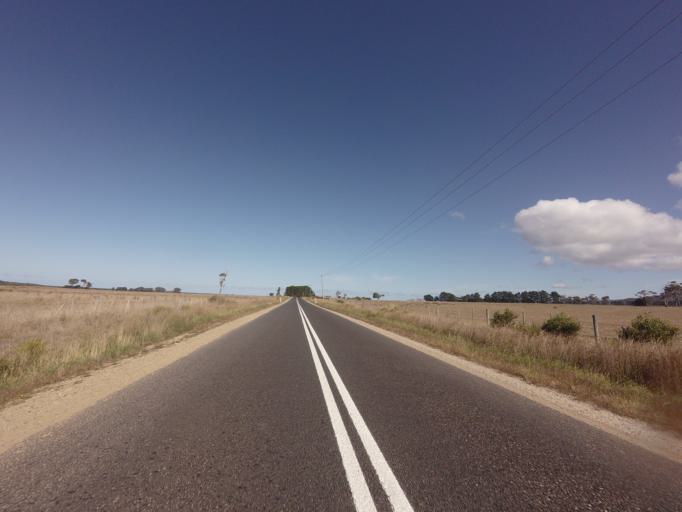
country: AU
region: Tasmania
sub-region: Break O'Day
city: St Helens
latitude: -41.7448
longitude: 148.2741
